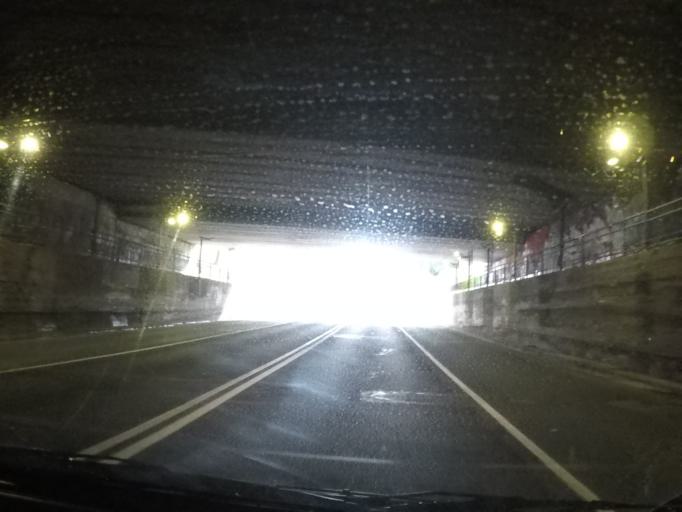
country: SK
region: Kosicky
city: Spisska Nova Ves
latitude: 48.9497
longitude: 20.5665
